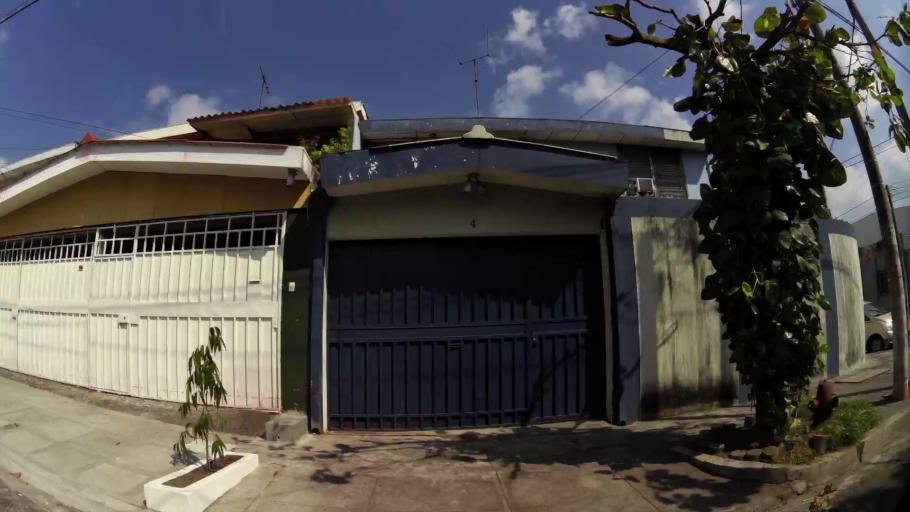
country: SV
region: San Salvador
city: Mejicanos
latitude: 13.7245
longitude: -89.2137
